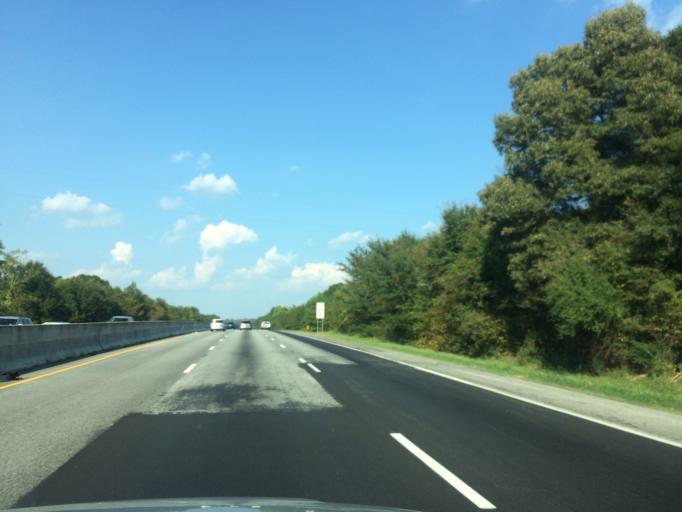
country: US
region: South Carolina
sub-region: Anderson County
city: Williamston
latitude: 34.6553
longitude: -82.5650
